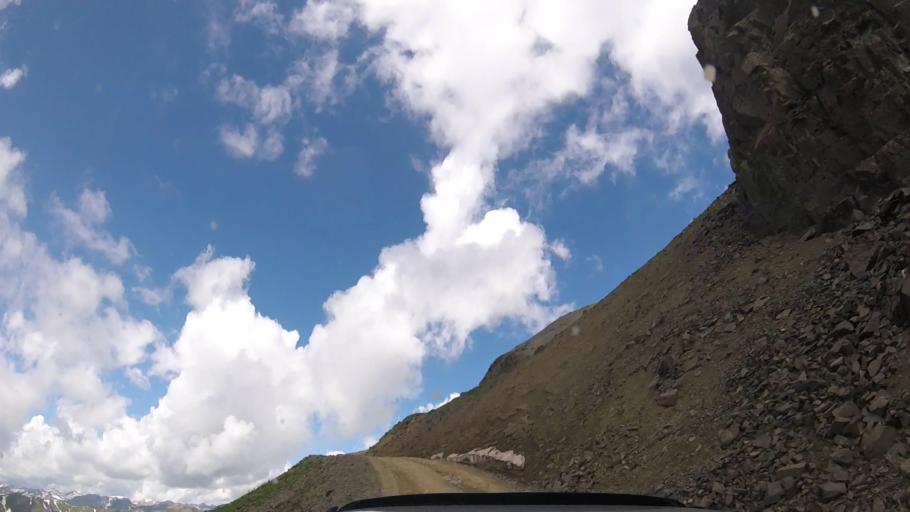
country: US
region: Colorado
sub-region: Ouray County
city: Ouray
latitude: 37.9660
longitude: -107.5844
